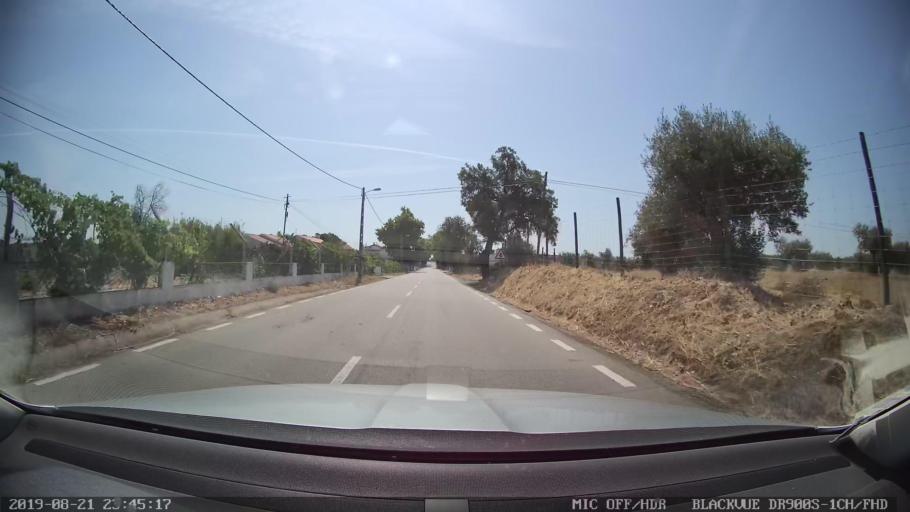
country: PT
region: Castelo Branco
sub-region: Idanha-A-Nova
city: Idanha-a-Nova
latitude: 39.8394
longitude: -7.2658
